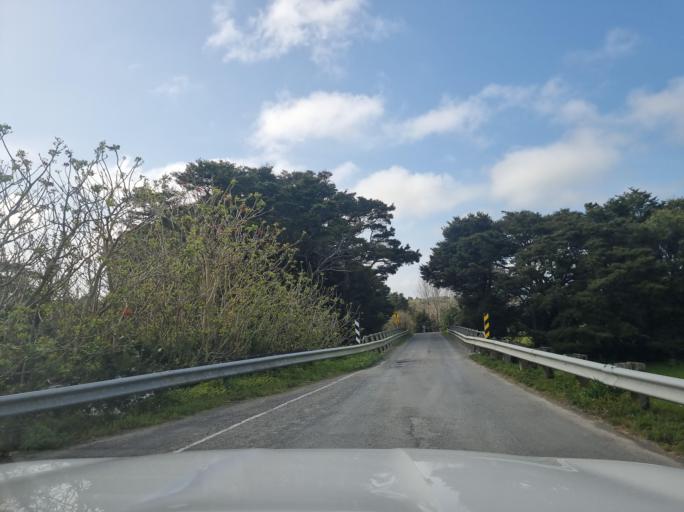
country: NZ
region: Northland
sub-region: Whangarei
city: Ruakaka
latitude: -36.0088
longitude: 174.4566
